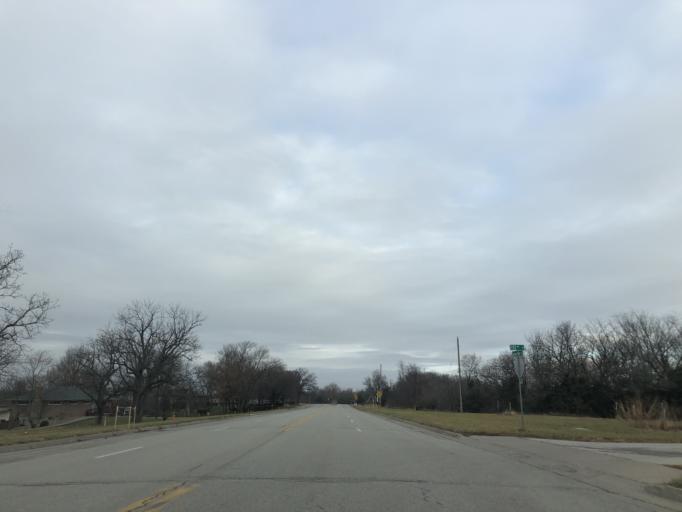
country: US
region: Kansas
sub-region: Johnson County
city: Gardner
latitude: 38.8520
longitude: -94.9354
